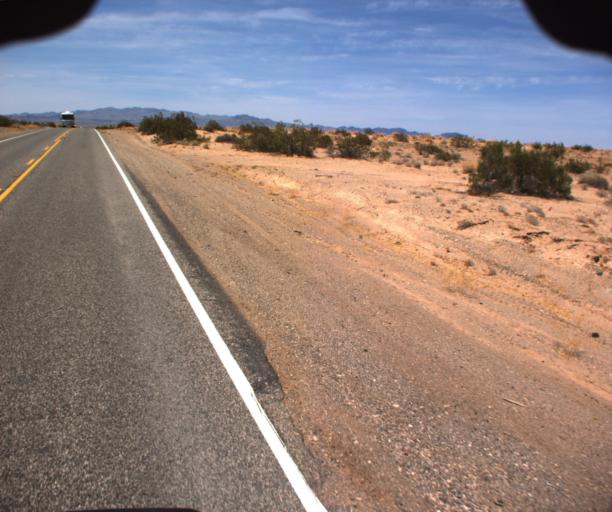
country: US
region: Arizona
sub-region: La Paz County
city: Parker
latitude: 34.0764
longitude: -114.2642
